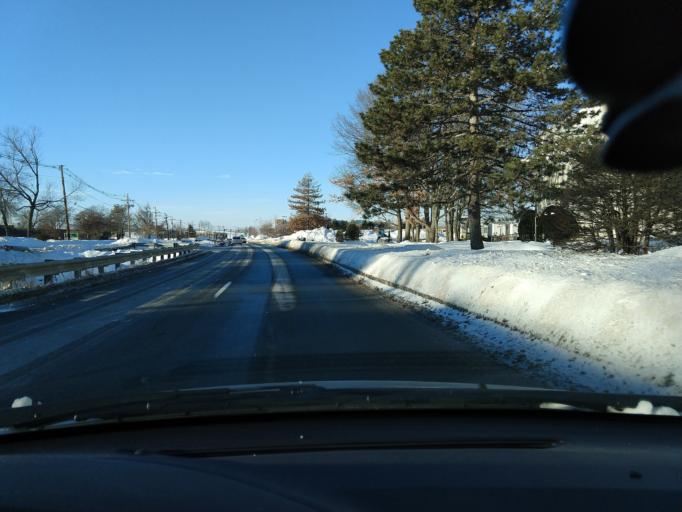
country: US
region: Massachusetts
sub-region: Middlesex County
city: Woburn
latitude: 42.5148
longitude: -71.1357
